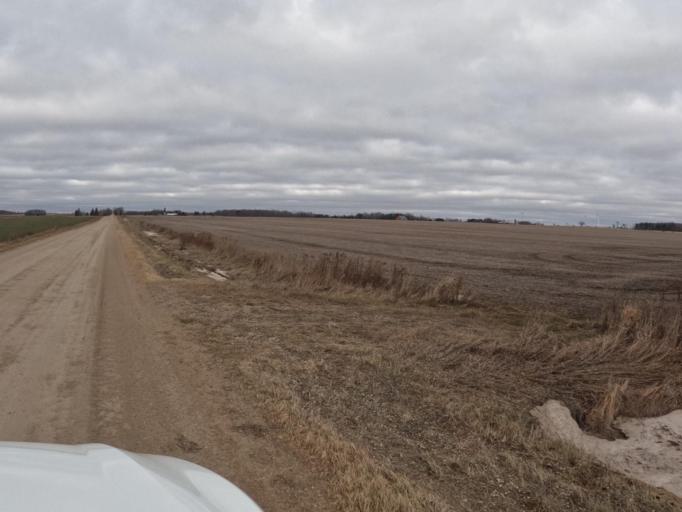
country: CA
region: Ontario
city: Shelburne
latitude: 43.8681
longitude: -80.4010
